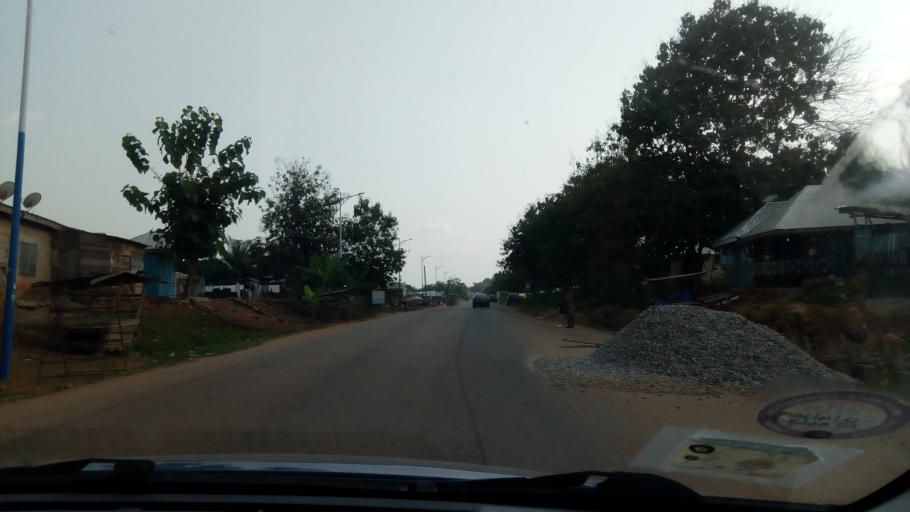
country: GH
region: Western
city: Bibiani
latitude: 6.7948
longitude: -2.5168
